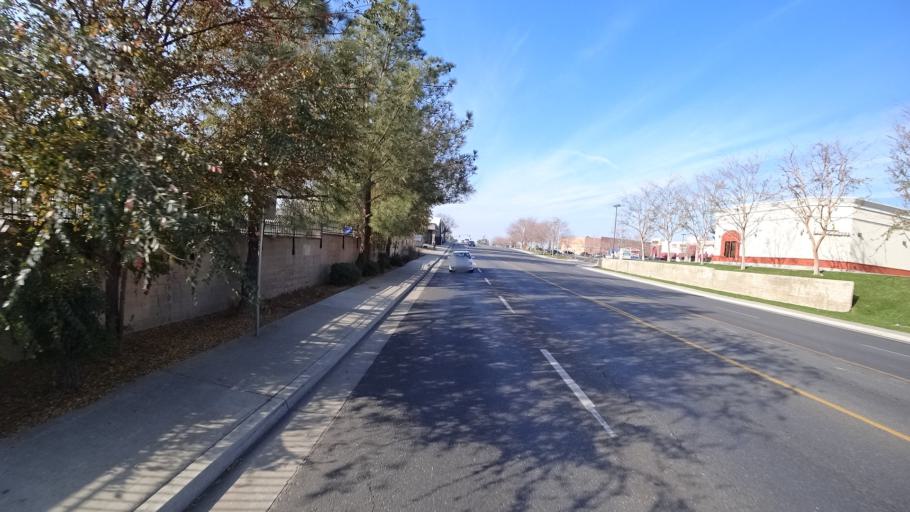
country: US
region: California
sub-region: Kern County
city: Bakersfield
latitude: 35.3902
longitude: -118.9649
